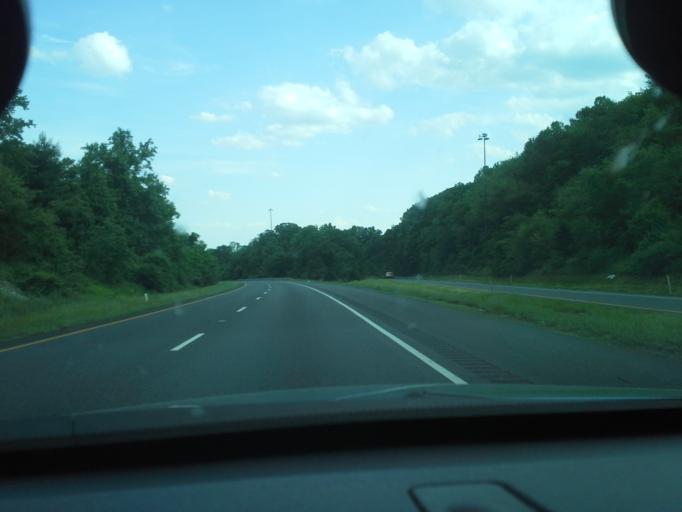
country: US
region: Maryland
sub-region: Frederick County
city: Braddock Heights
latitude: 39.4308
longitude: -77.4896
